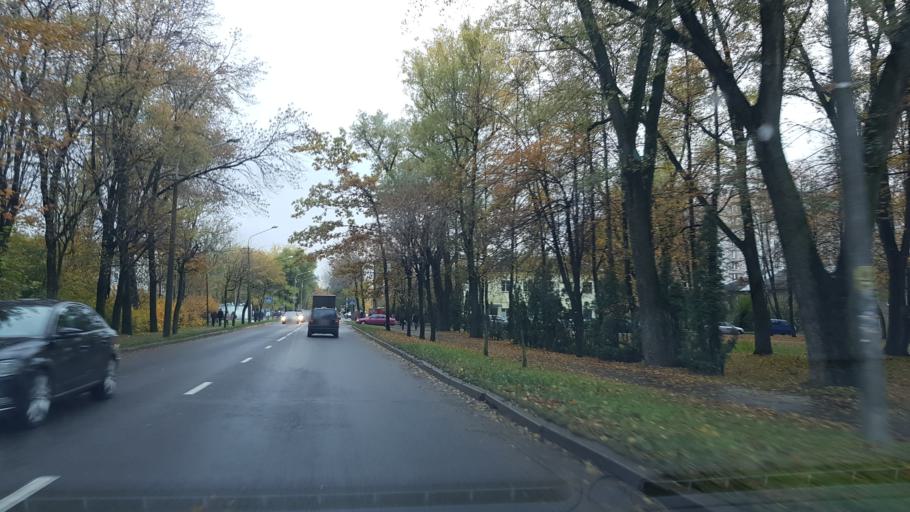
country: BY
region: Minsk
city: Syenitsa
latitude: 53.8458
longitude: 27.5476
